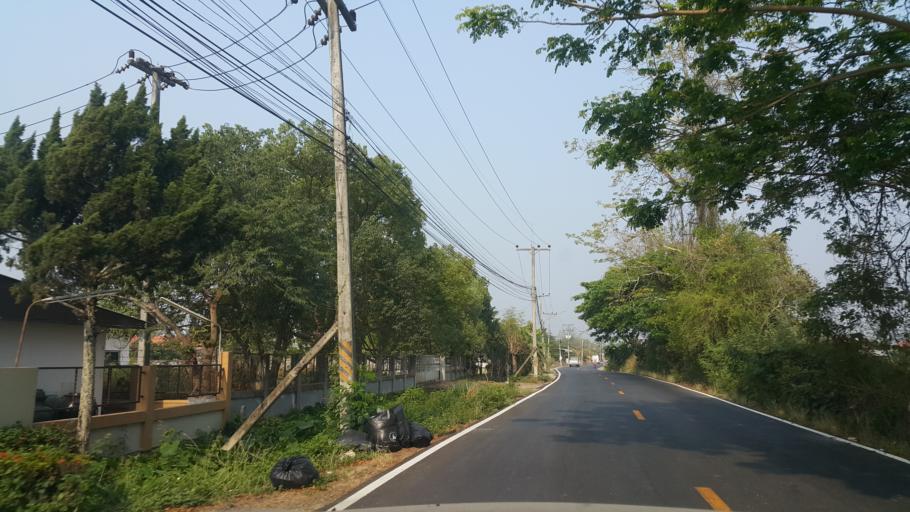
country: TH
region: Chiang Mai
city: Saraphi
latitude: 18.6823
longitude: 99.0716
